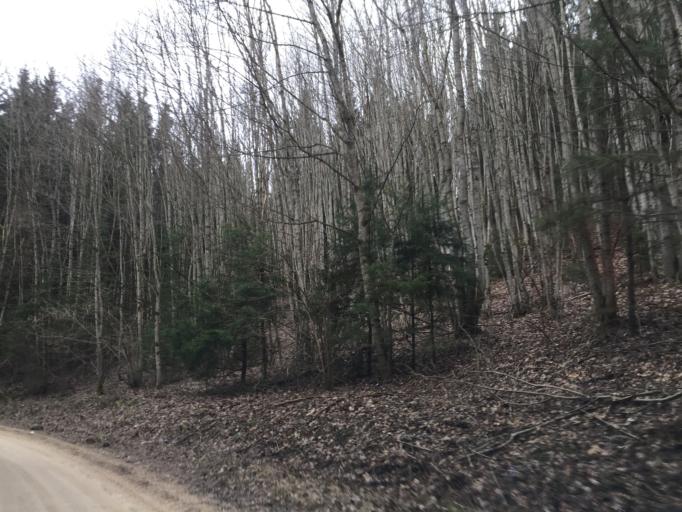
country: LV
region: Ilukste
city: Ilukste
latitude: 55.9016
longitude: 26.3458
